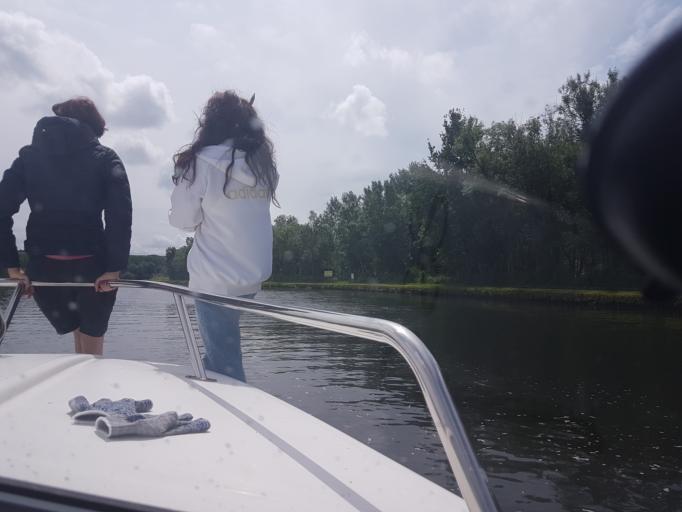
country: FR
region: Bourgogne
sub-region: Departement de l'Yonne
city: Augy
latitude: 47.7806
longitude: 3.6026
